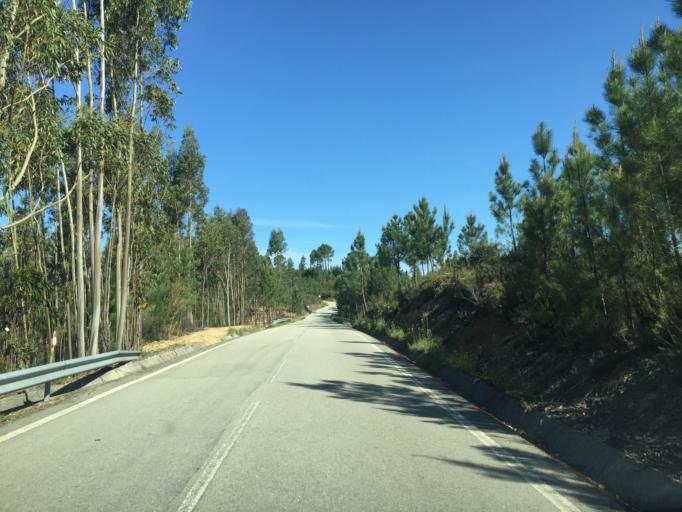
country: PT
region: Coimbra
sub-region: Pampilhosa da Serra
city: Pampilhosa da Serra
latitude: 40.0799
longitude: -7.7942
